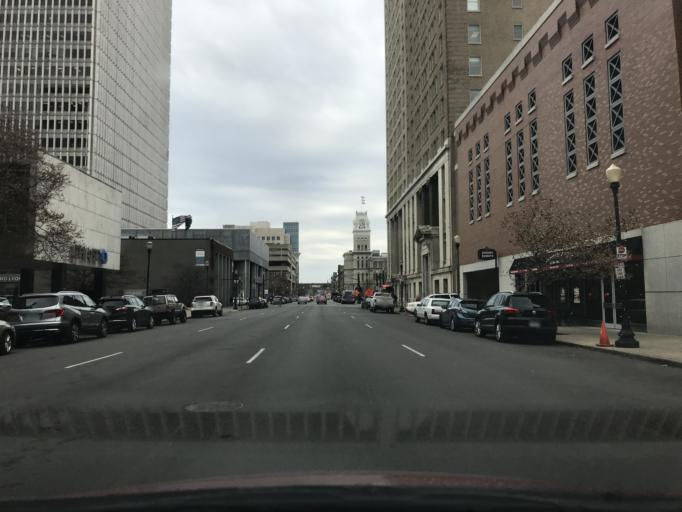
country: US
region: Kentucky
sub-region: Jefferson County
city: Louisville
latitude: 38.2539
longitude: -85.7575
